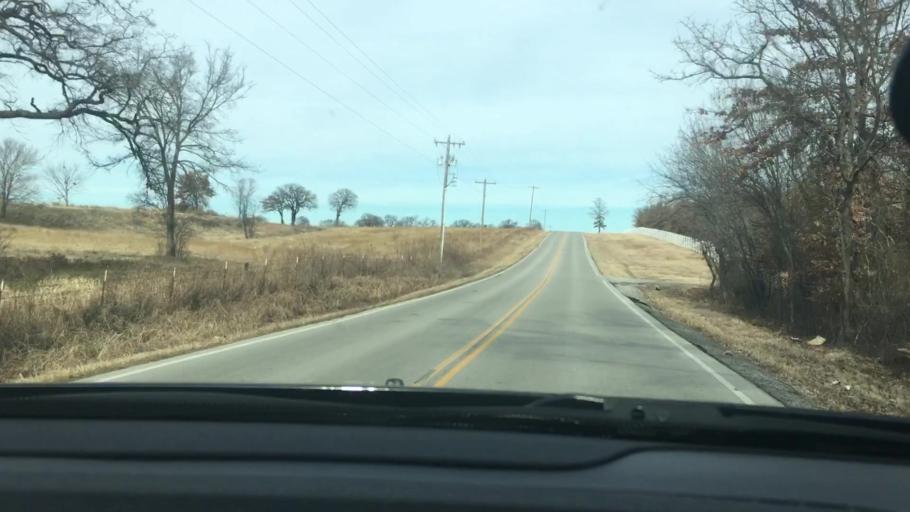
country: US
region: Oklahoma
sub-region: Carter County
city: Ardmore
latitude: 34.1811
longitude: -97.0731
